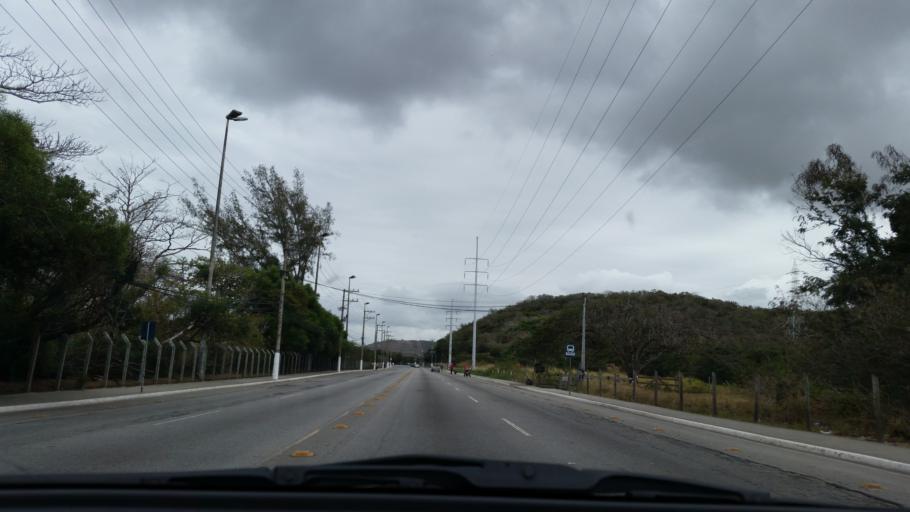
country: BR
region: Rio de Janeiro
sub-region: Cabo Frio
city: Cabo Frio
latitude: -22.8672
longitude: -42.0298
